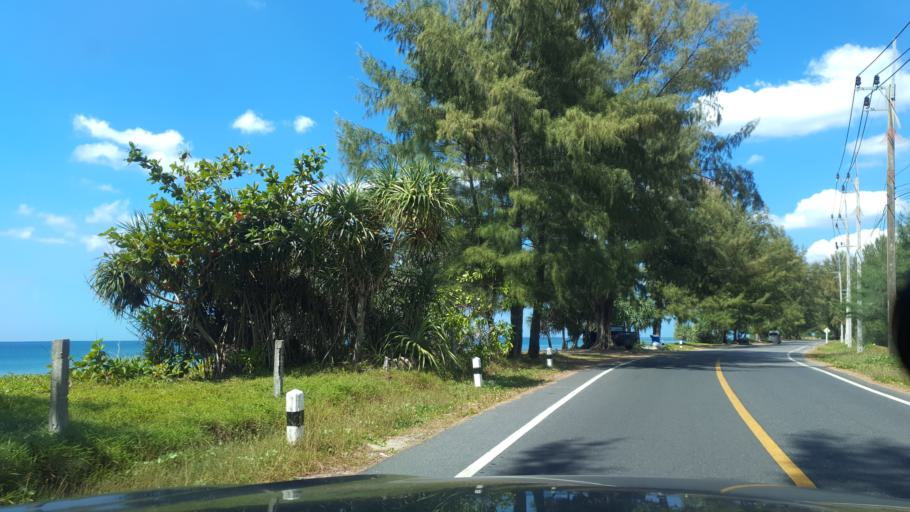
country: TH
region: Phangnga
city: Thai Mueang
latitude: 8.2951
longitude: 98.2722
